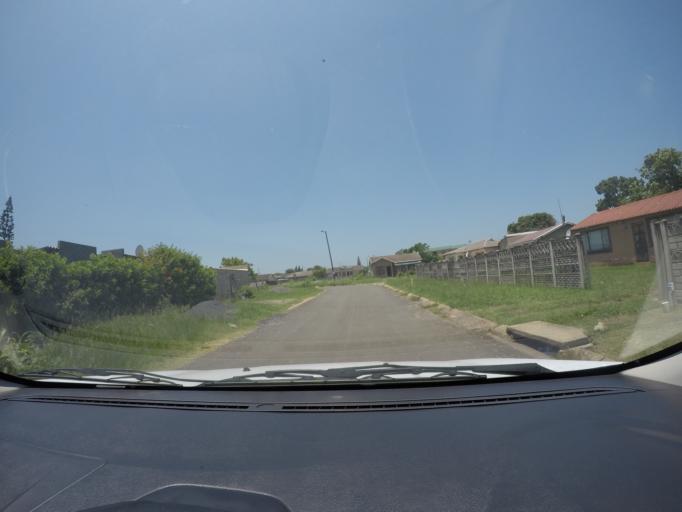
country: ZA
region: KwaZulu-Natal
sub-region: uThungulu District Municipality
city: eSikhawini
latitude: -28.8765
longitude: 31.8978
